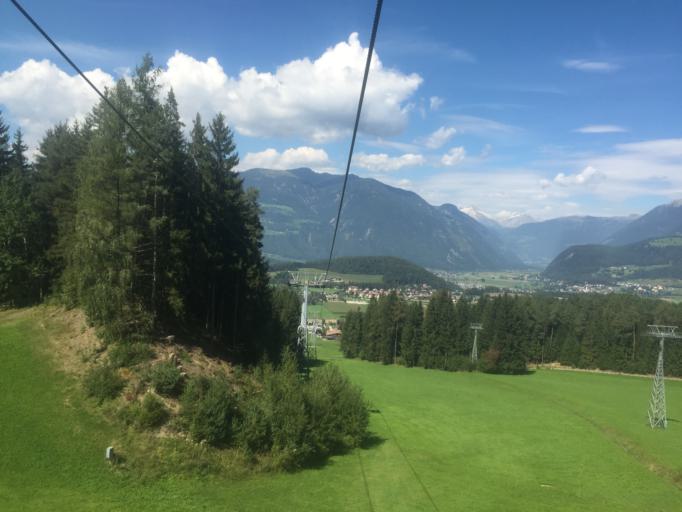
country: IT
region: Trentino-Alto Adige
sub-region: Bolzano
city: Riscone
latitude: 46.7650
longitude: 11.9444
